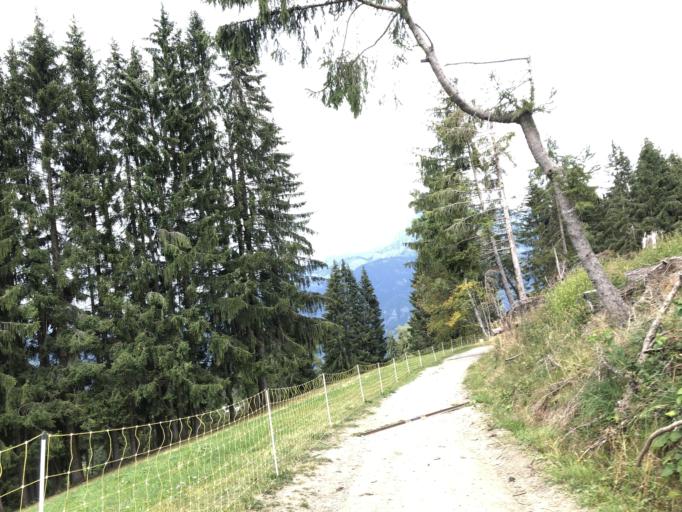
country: FR
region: Rhone-Alpes
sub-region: Departement de la Haute-Savoie
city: Combloux
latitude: 45.8892
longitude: 6.6217
